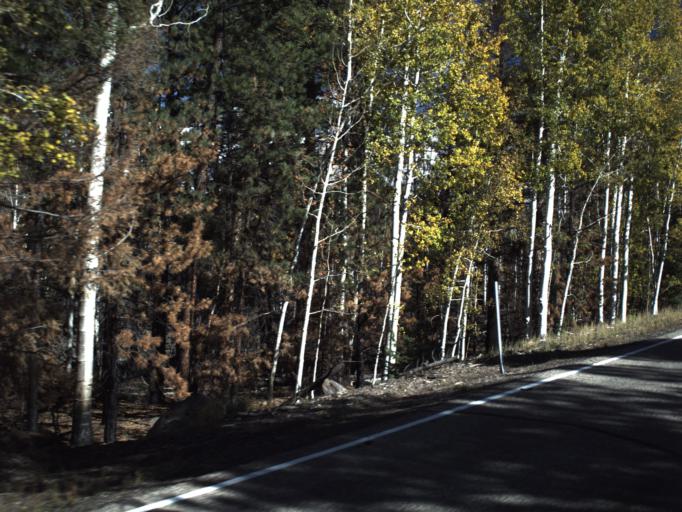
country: US
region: Utah
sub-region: Iron County
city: Parowan
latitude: 37.6659
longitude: -112.6679
